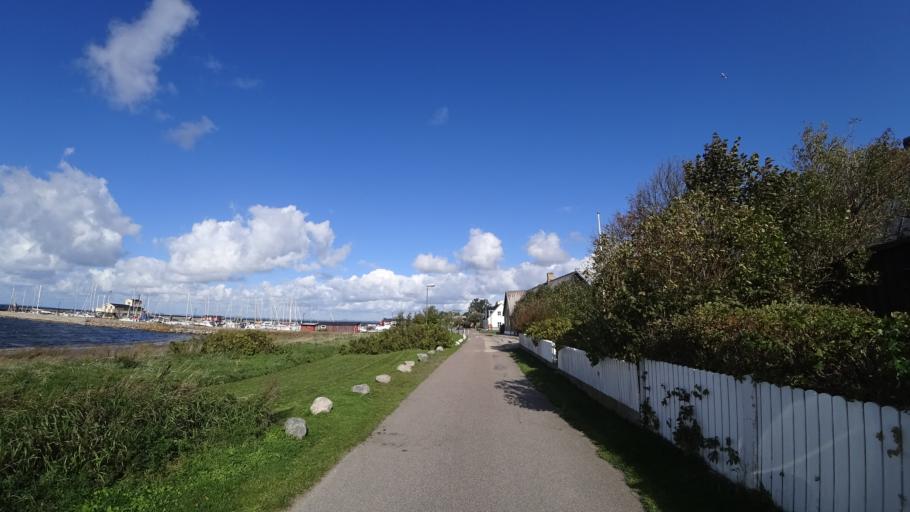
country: SE
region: Skane
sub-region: Kavlinge Kommun
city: Hofterup
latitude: 55.7547
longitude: 12.9045
